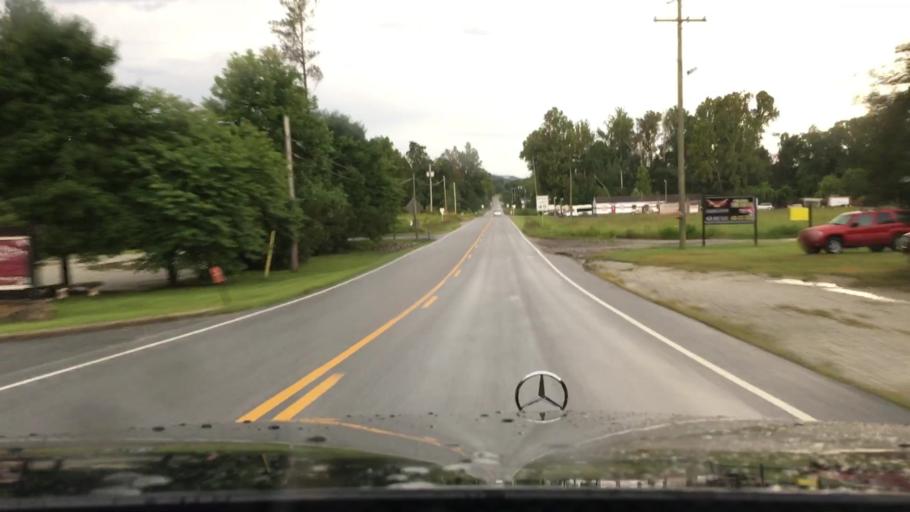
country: US
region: Virginia
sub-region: Amherst County
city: Amherst
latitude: 37.7082
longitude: -79.0232
